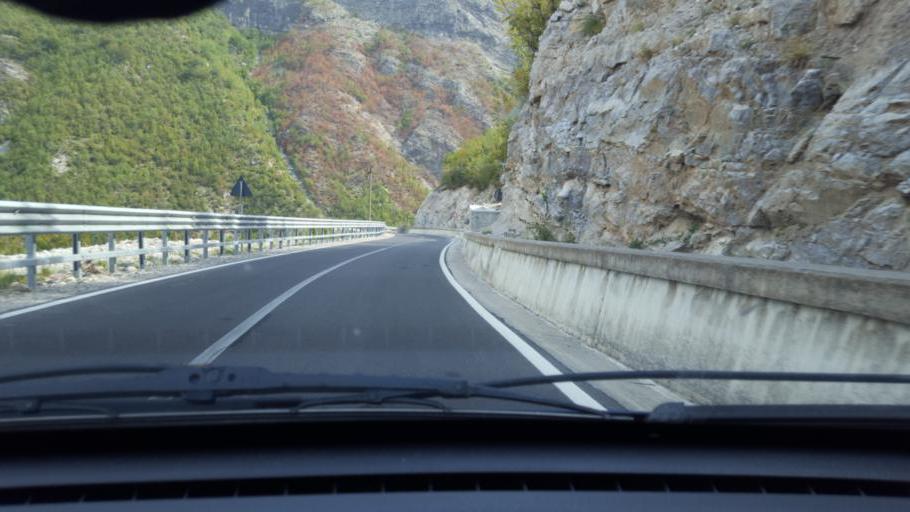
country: AL
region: Shkoder
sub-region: Rrethi i Malesia e Madhe
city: Kastrat
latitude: 42.4157
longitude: 19.5073
